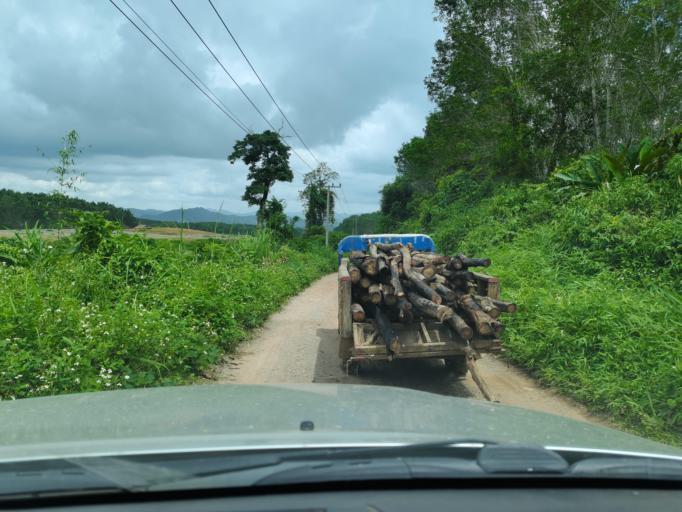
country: LA
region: Loungnamtha
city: Muang Long
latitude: 20.7005
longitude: 101.0353
